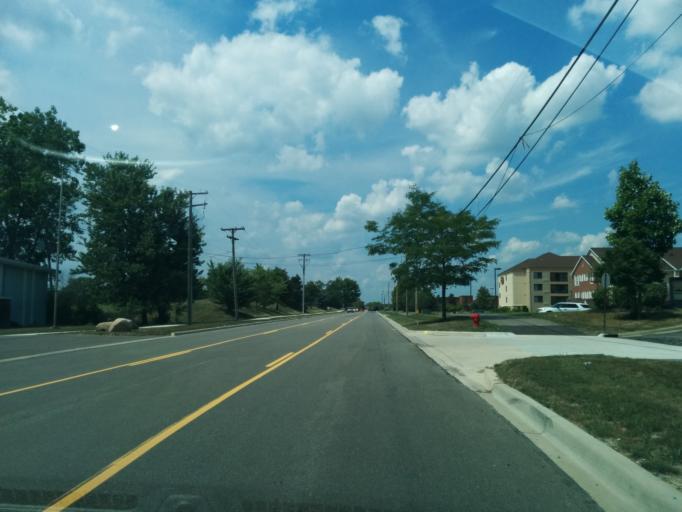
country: US
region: Michigan
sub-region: Oakland County
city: Novi
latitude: 42.4814
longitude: -83.4657
